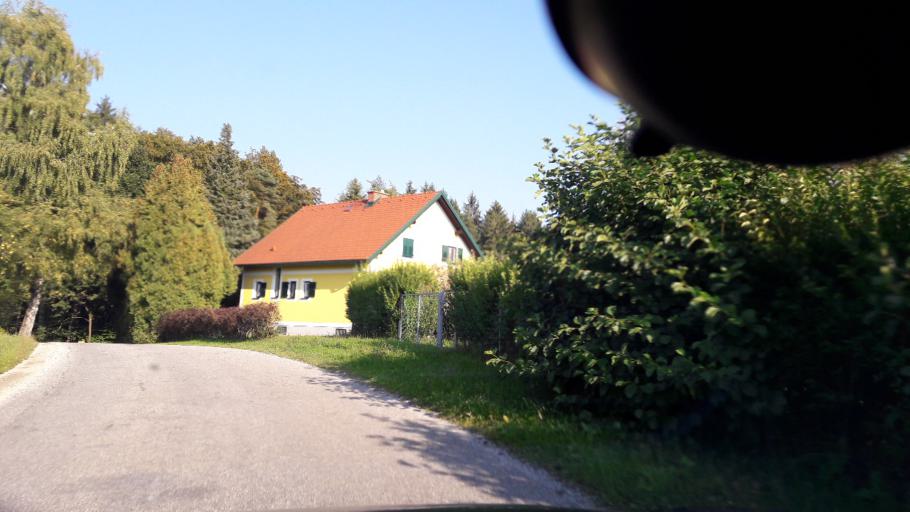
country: AT
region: Styria
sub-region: Politischer Bezirk Graz-Umgebung
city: Stiwoll
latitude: 47.1015
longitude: 15.2323
